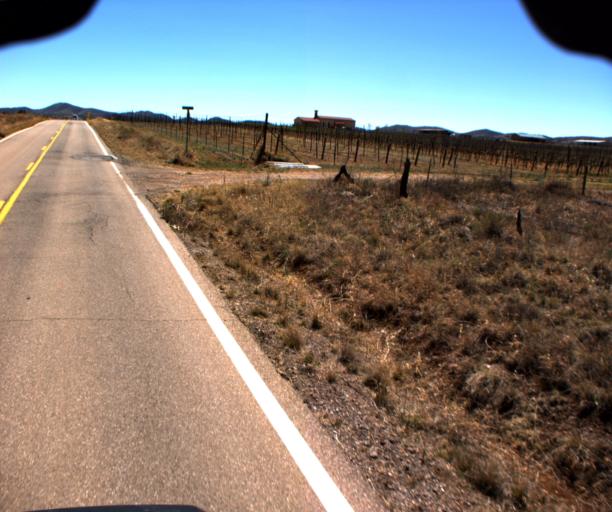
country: US
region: Arizona
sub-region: Cochise County
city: Huachuca City
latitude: 31.6119
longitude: -110.5871
